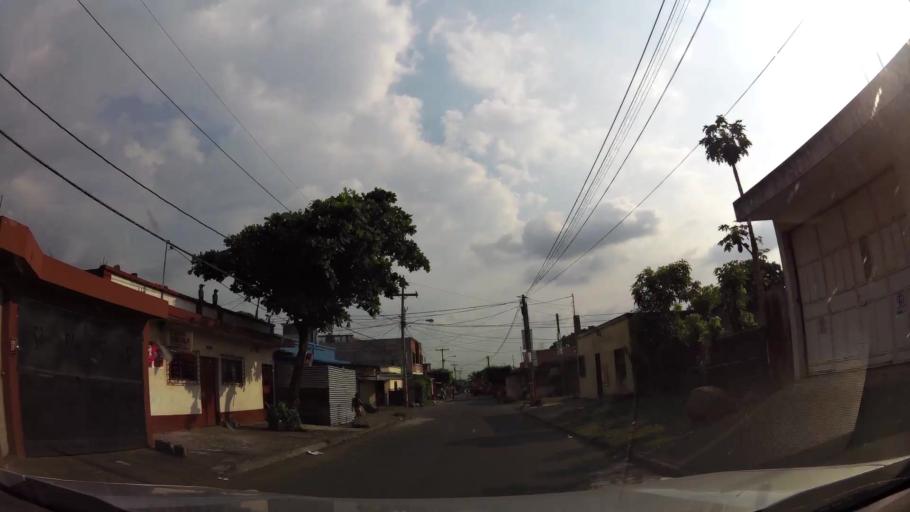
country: GT
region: Escuintla
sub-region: Municipio de Escuintla
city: Escuintla
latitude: 14.3144
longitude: -90.7965
